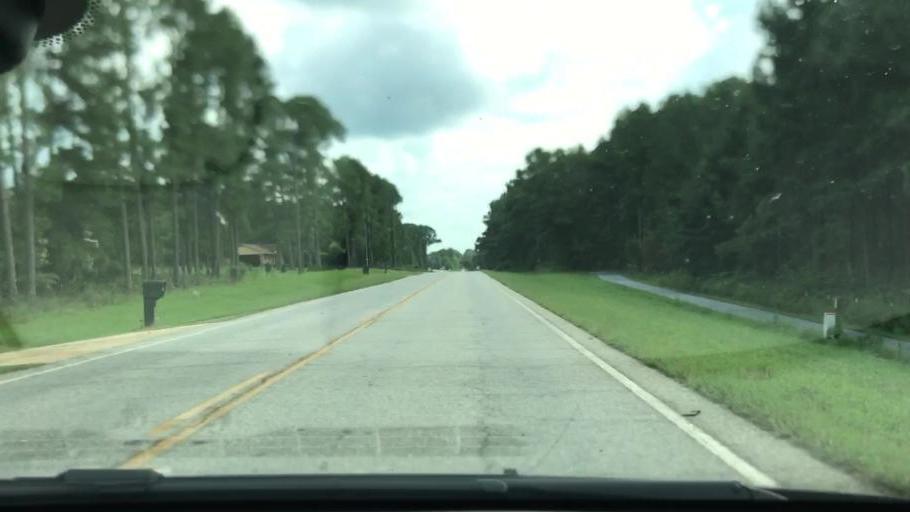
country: US
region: Georgia
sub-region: Clay County
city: Fort Gaines
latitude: 31.6586
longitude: -85.0474
